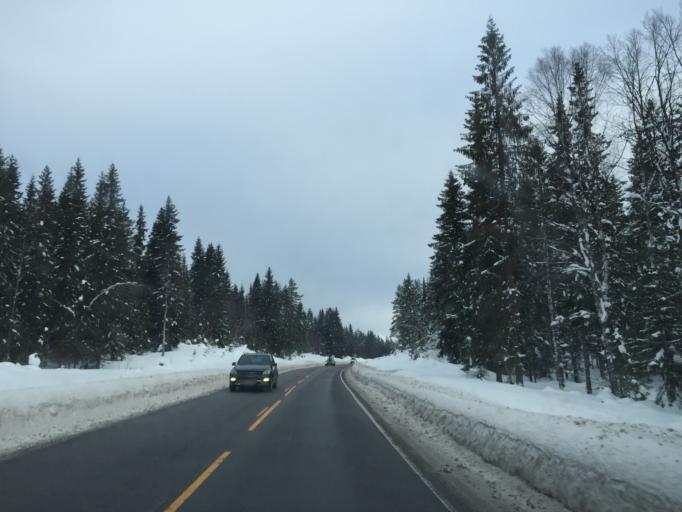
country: NO
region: Hedmark
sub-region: Trysil
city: Innbygda
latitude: 61.1701
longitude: 12.1592
